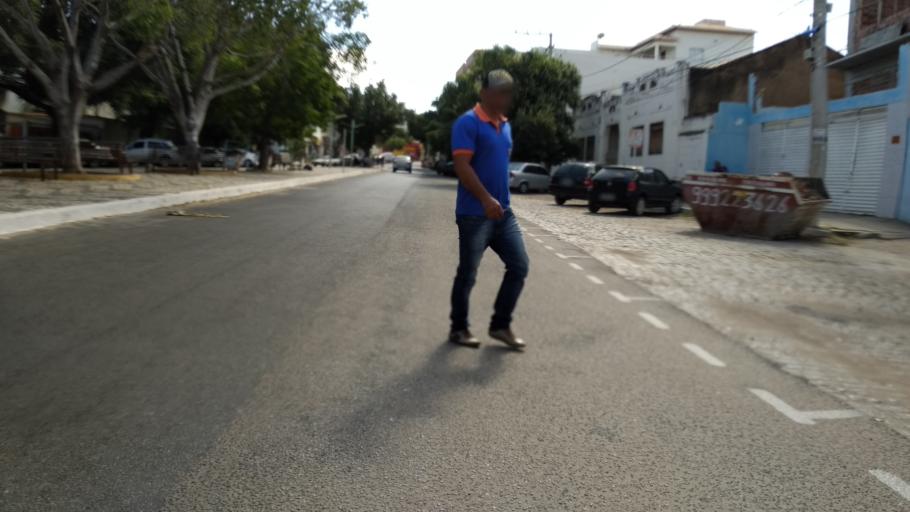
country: BR
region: Bahia
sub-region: Guanambi
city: Guanambi
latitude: -14.2300
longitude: -42.7804
